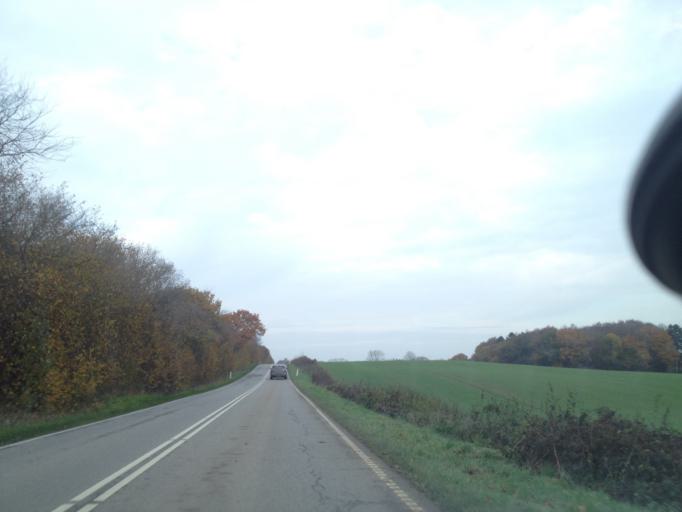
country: DK
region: South Denmark
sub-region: Assens Kommune
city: Vissenbjerg
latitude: 55.4502
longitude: 10.1227
